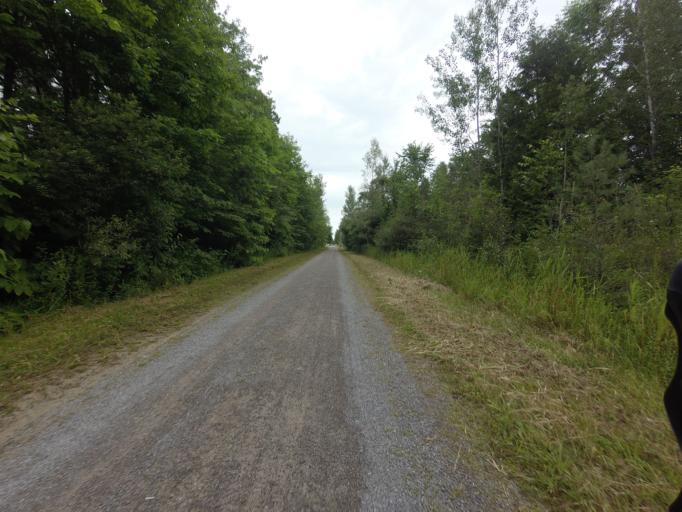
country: CA
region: Ontario
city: Ottawa
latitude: 45.2350
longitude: -75.6190
